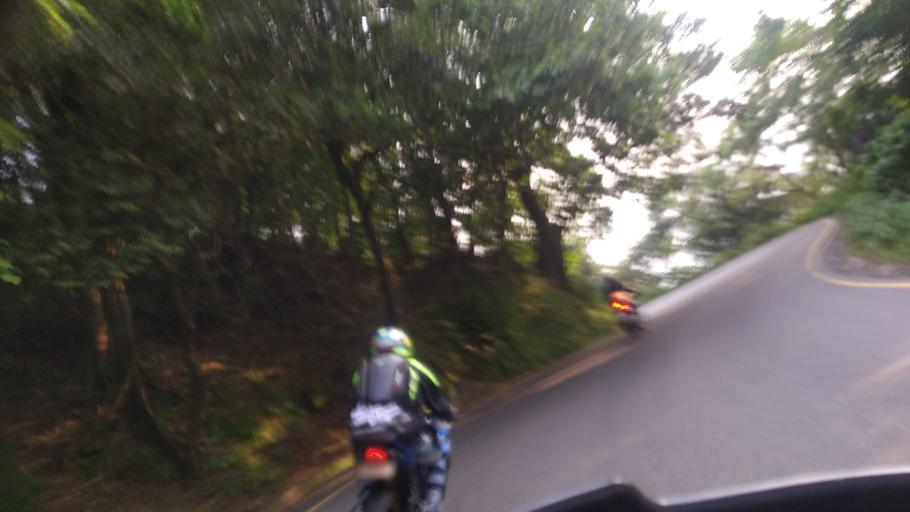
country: IN
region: Kerala
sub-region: Wayanad
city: Kalpetta
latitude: 11.5137
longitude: 76.0151
